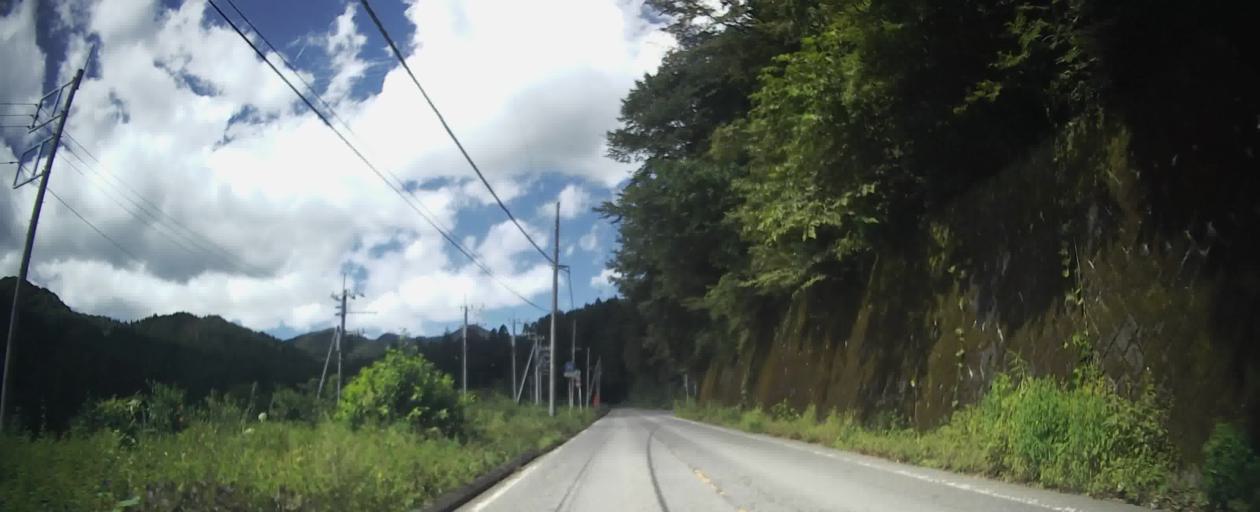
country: JP
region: Gunma
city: Kanekomachi
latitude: 36.4382
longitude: 138.9154
